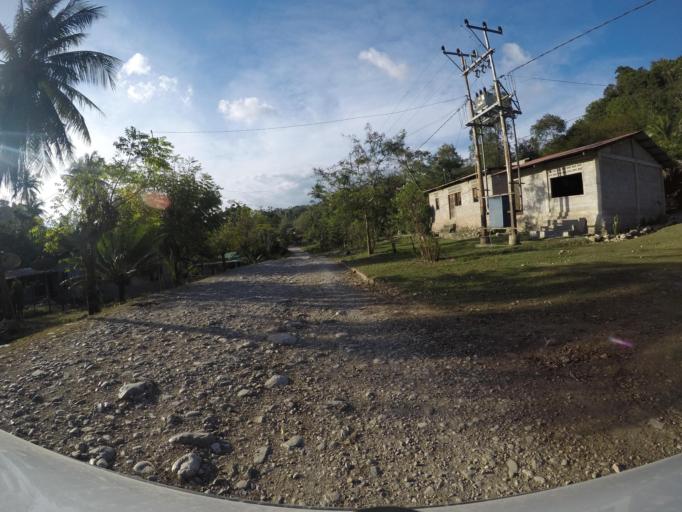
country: TL
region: Viqueque
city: Viqueque
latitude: -8.7966
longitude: 126.5608
